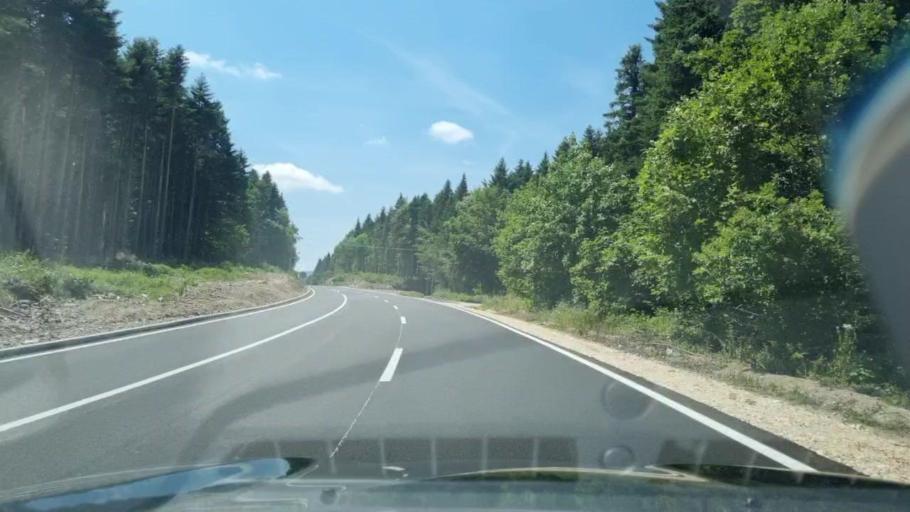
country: BA
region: Federation of Bosnia and Herzegovina
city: Sanica
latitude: 44.5579
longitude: 16.6610
